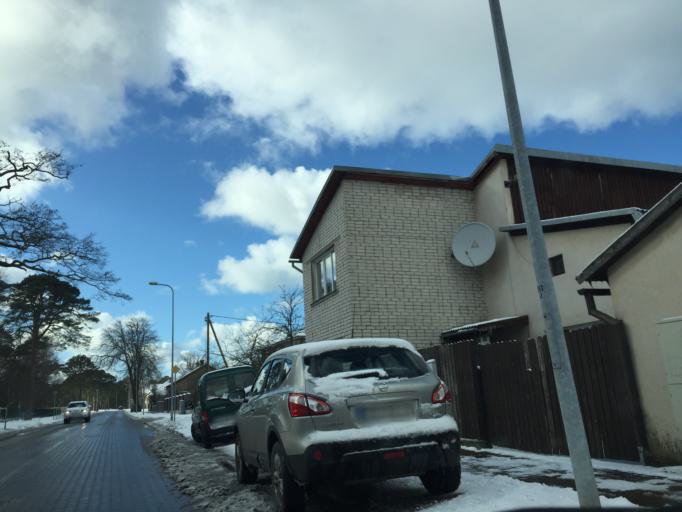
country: LV
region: Ventspils
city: Ventspils
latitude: 57.3782
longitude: 21.5567
